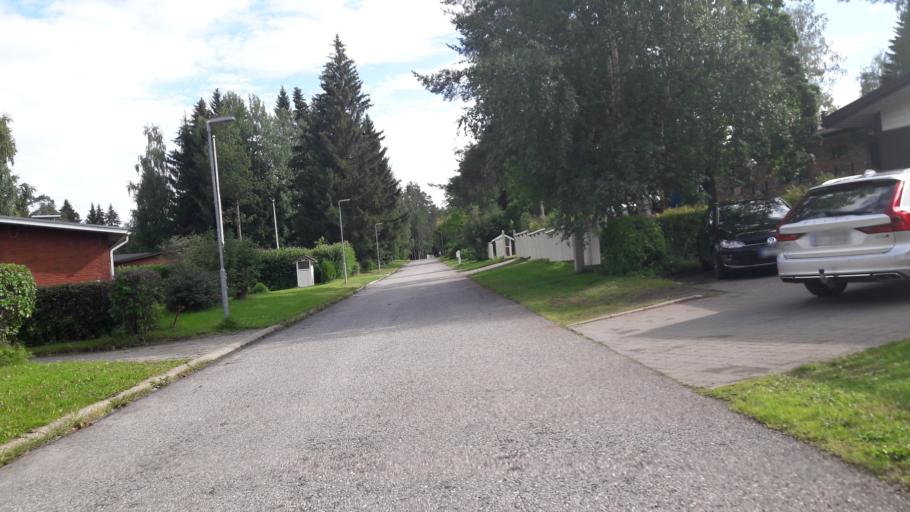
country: FI
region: North Karelia
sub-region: Joensuu
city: Joensuu
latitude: 62.5873
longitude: 29.7983
